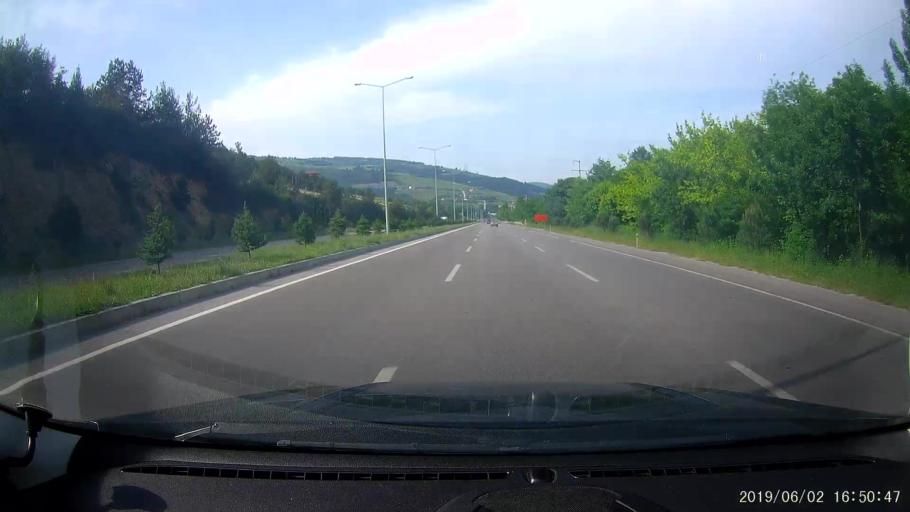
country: TR
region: Samsun
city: Taflan
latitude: 41.2618
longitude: 36.1754
